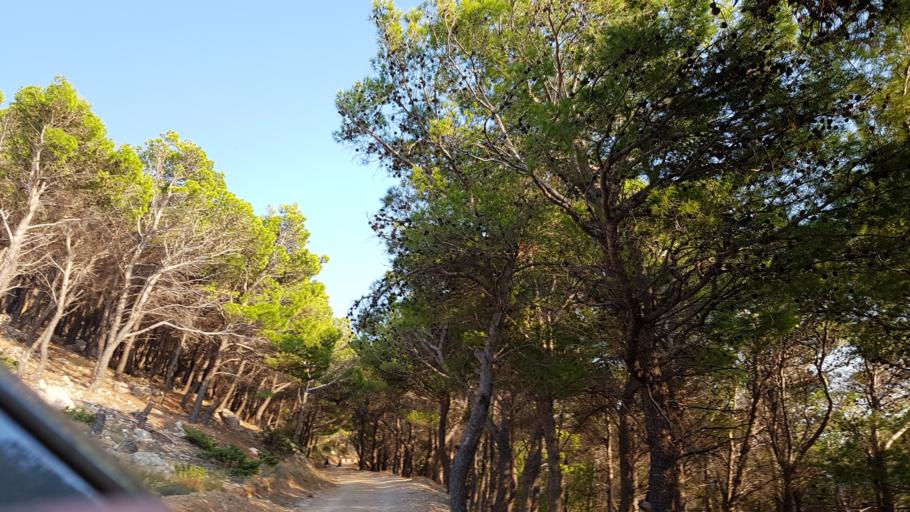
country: HR
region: Splitsko-Dalmatinska
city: Donja Brela
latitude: 43.3895
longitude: 16.8964
